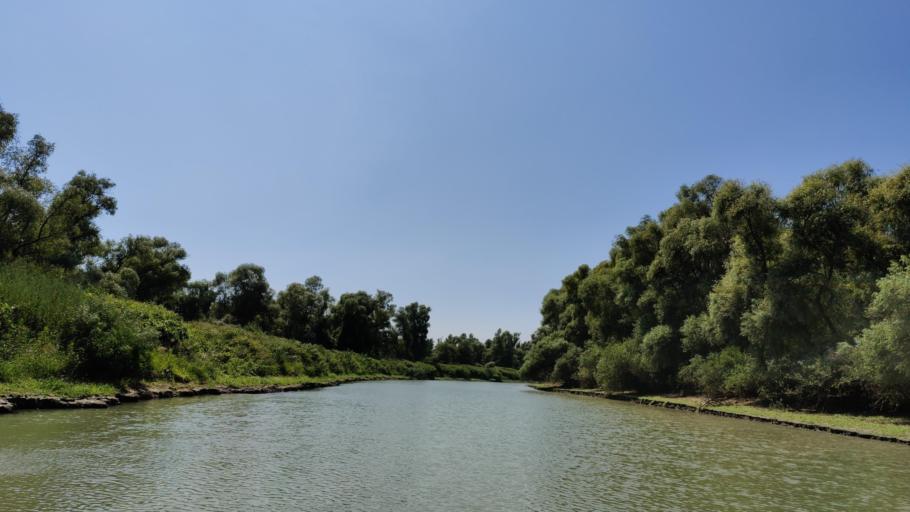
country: RO
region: Tulcea
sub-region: Comuna Pardina
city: Pardina
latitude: 45.2555
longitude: 28.9563
